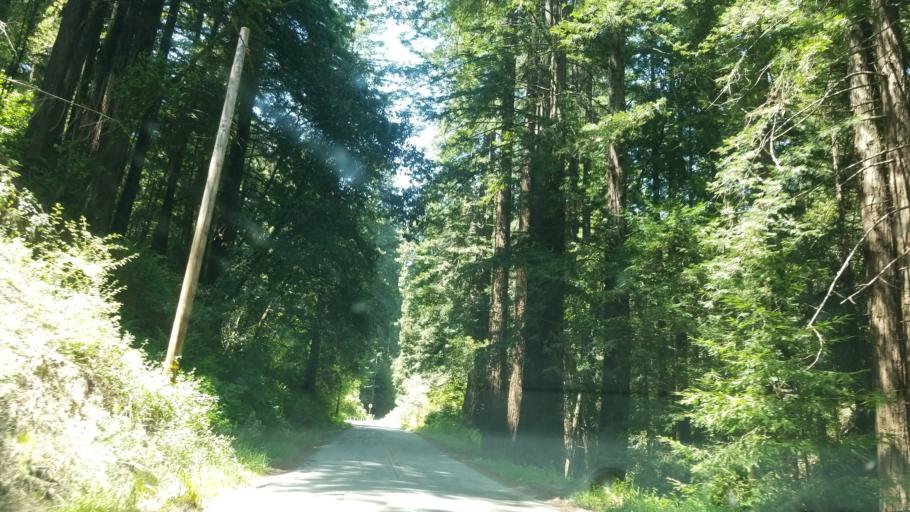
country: US
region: California
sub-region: Santa Cruz County
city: Amesti
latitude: 37.0099
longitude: -121.7502
